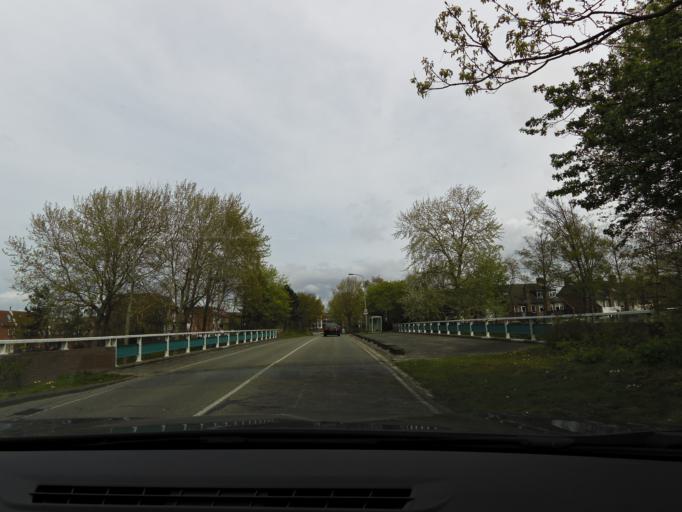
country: NL
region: South Holland
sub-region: Gemeente Katwijk
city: Katwijk aan den Rijn
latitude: 52.2095
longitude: 4.4238
